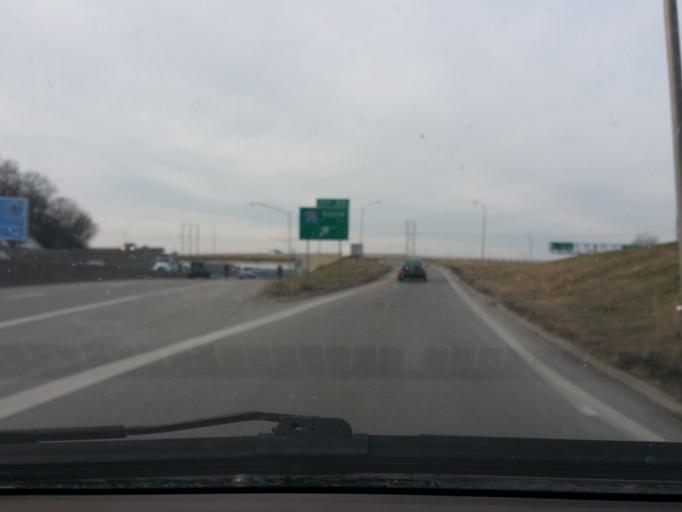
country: US
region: Missouri
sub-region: Jackson County
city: Kansas City
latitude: 39.1071
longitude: -94.5887
